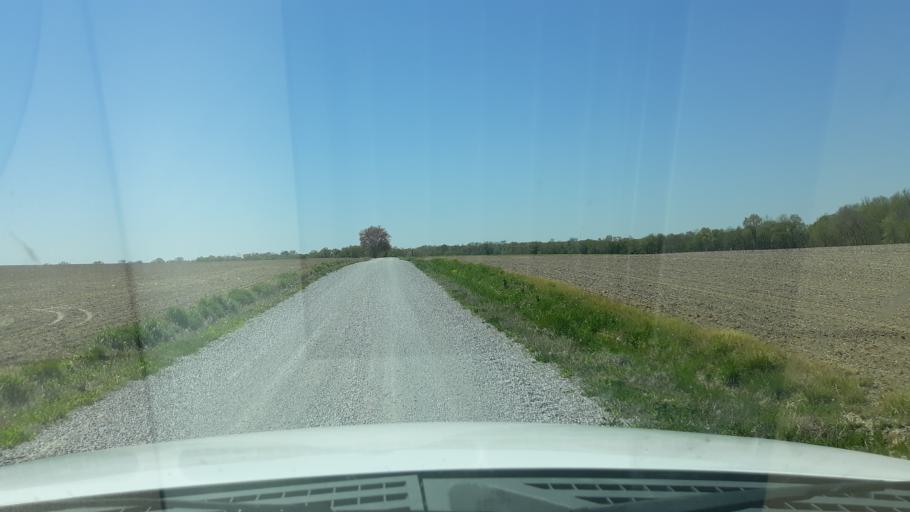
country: US
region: Illinois
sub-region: Saline County
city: Harrisburg
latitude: 37.8922
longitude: -88.6705
